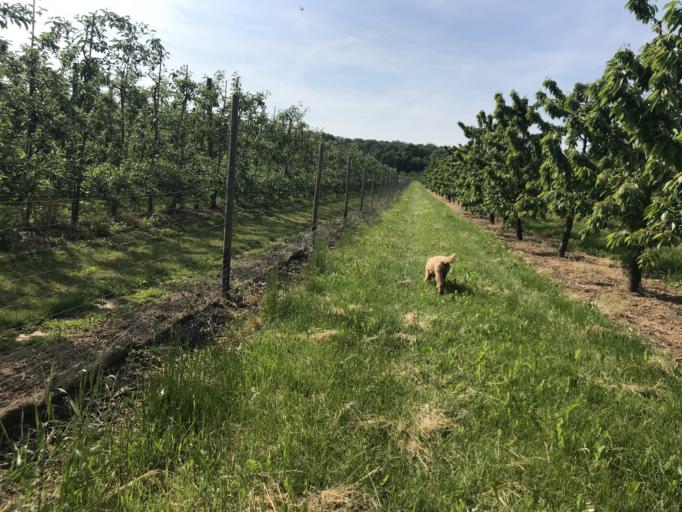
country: DE
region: Rheinland-Pfalz
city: Ober-Olm
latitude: 49.9713
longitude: 8.1733
